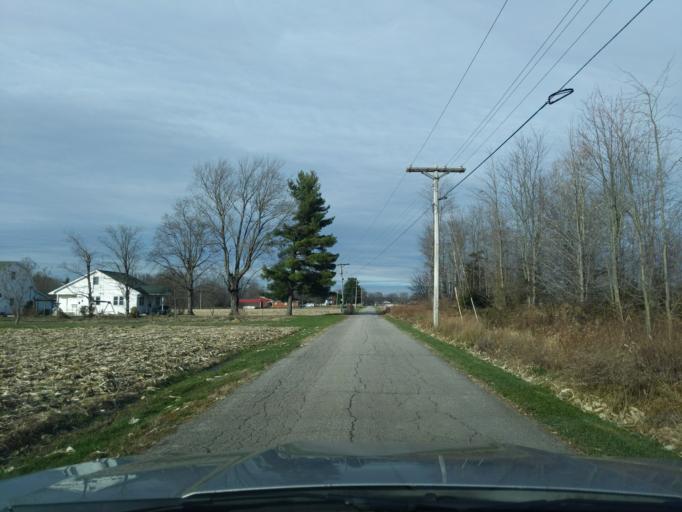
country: US
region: Indiana
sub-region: Decatur County
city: Greensburg
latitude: 39.2046
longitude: -85.4329
